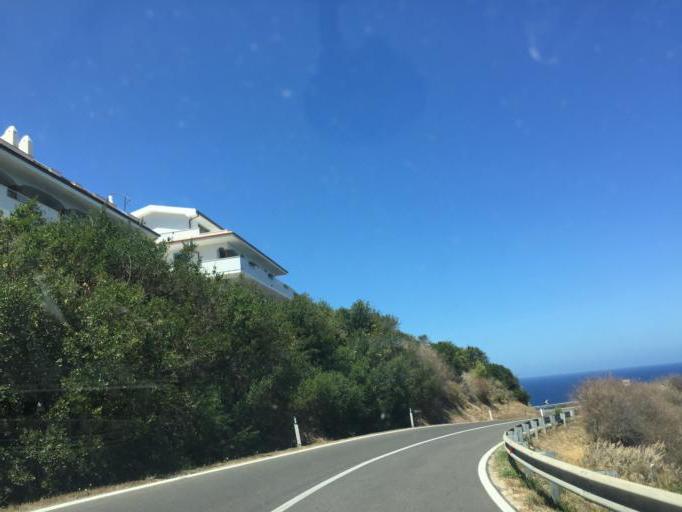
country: IT
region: Sardinia
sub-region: Provincia di Sassari
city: Castelsardo
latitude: 40.9109
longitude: 8.7270
